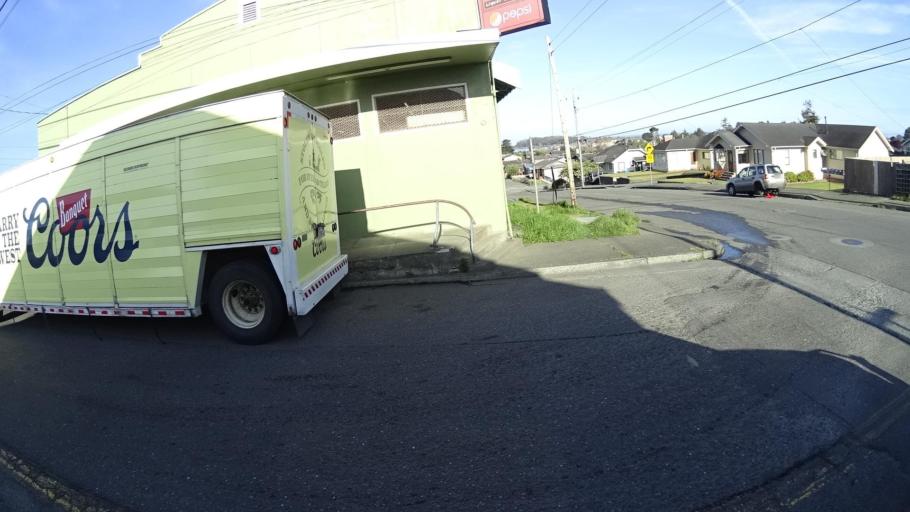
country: US
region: California
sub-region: Humboldt County
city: Bayview
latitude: 40.7731
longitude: -124.1820
